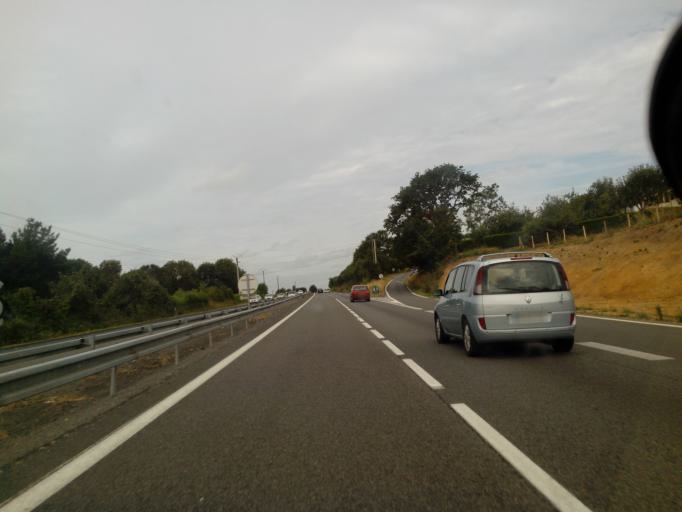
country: FR
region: Brittany
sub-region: Departement du Morbihan
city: Muzillac
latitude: 47.5495
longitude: -2.4707
